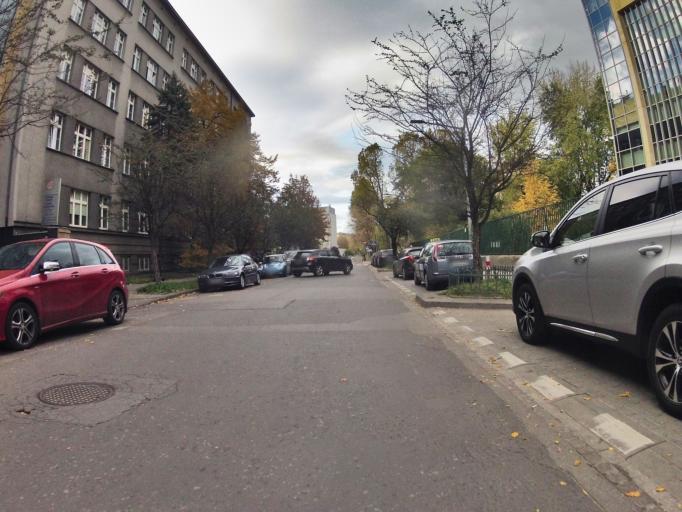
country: PL
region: Lesser Poland Voivodeship
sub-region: Krakow
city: Krakow
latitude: 50.0615
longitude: 19.9215
